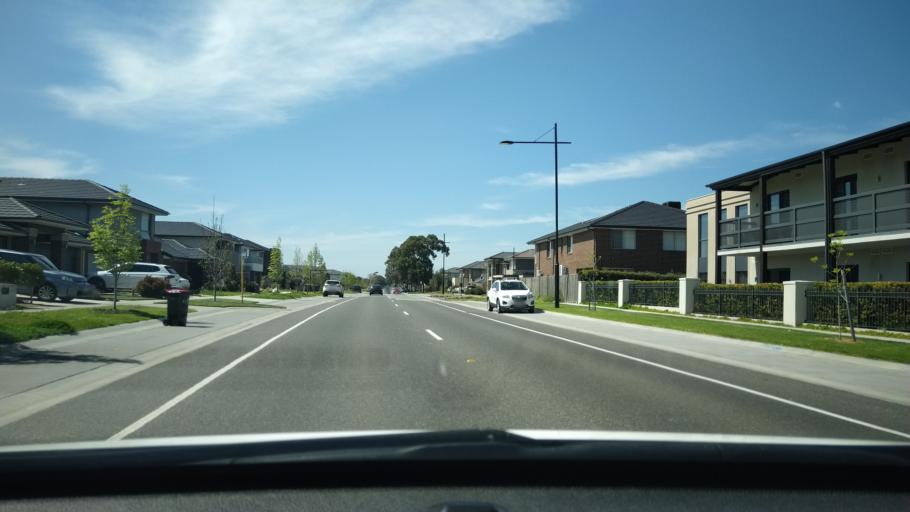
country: AU
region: Victoria
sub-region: Greater Dandenong
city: Keysborough
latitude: -38.0012
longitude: 145.1681
